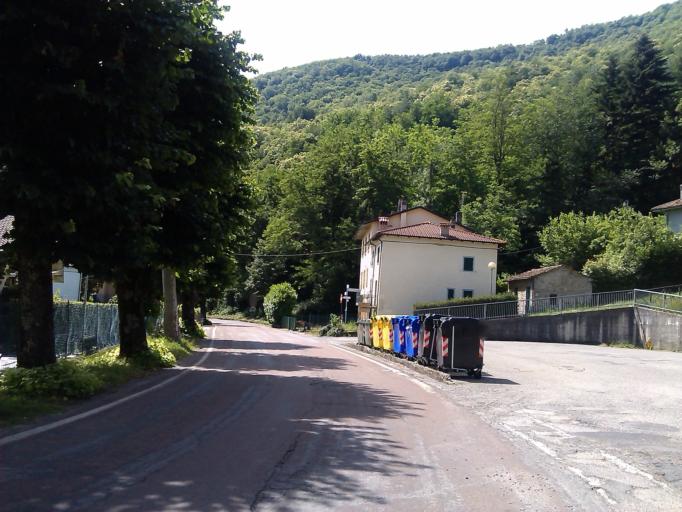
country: IT
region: Tuscany
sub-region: Provincia di Pistoia
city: Sambuca Pistoiese
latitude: 44.1178
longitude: 11.0283
